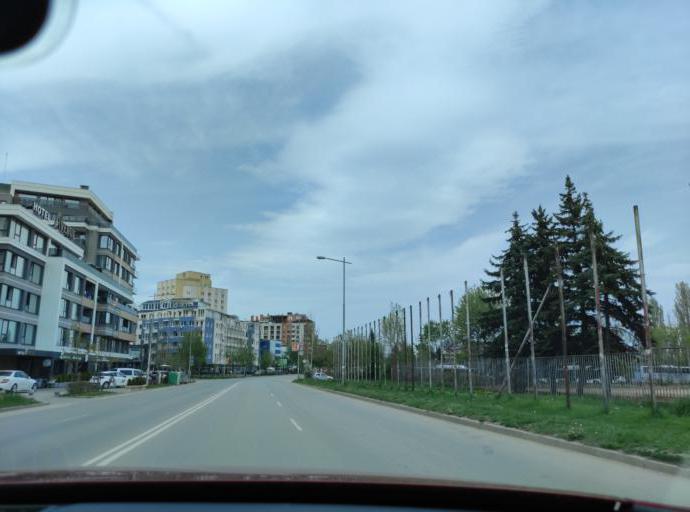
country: BG
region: Sofia-Capital
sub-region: Stolichna Obshtina
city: Sofia
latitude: 42.6460
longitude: 23.3453
